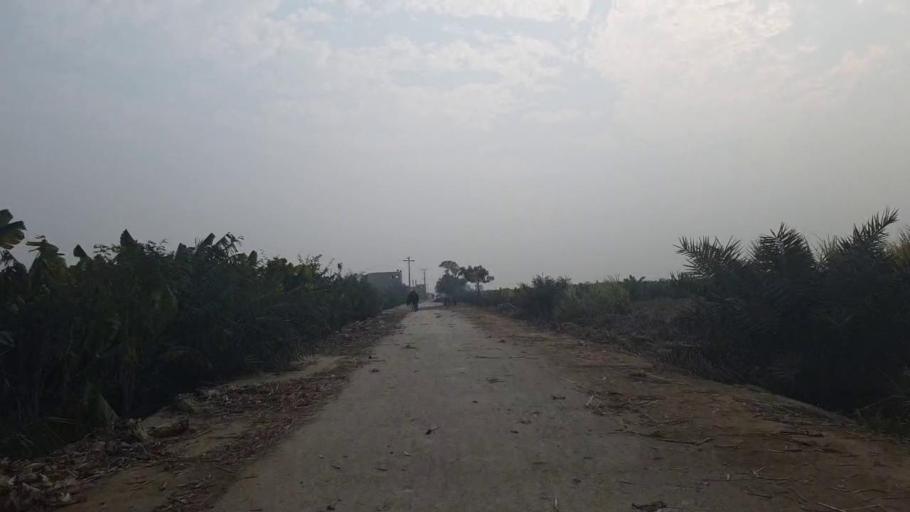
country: PK
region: Sindh
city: Berani
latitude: 25.8009
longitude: 68.7322
